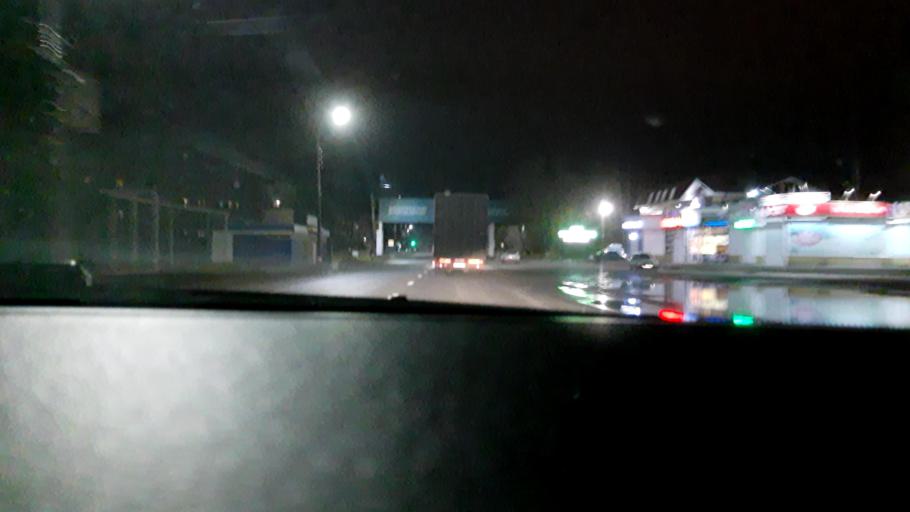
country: RU
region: Nizjnij Novgorod
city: Novaya Balakhna
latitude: 56.5207
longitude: 43.5720
